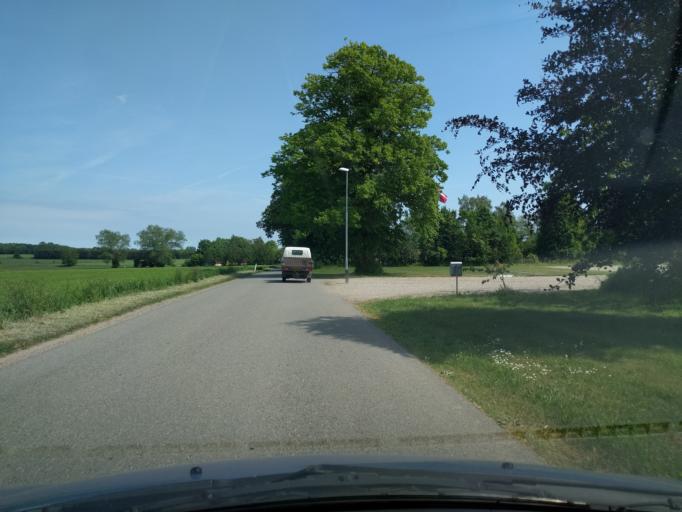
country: DK
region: South Denmark
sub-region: Nyborg Kommune
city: Ullerslev
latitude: 55.3957
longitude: 10.6195
